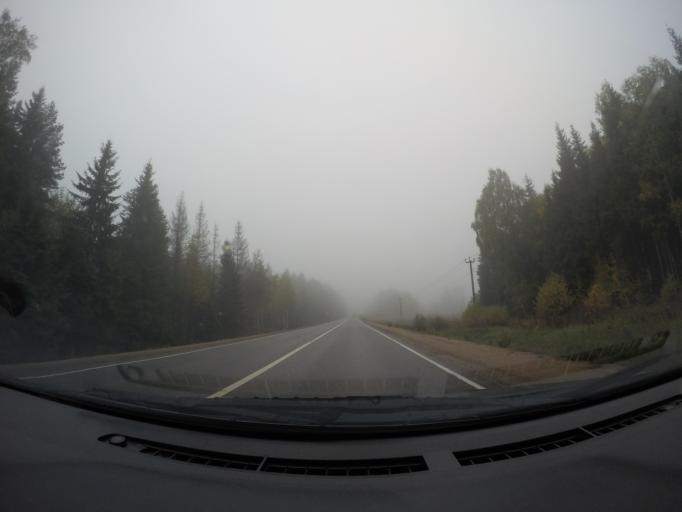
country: RU
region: Moskovskaya
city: Ruza
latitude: 55.7231
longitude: 36.2799
